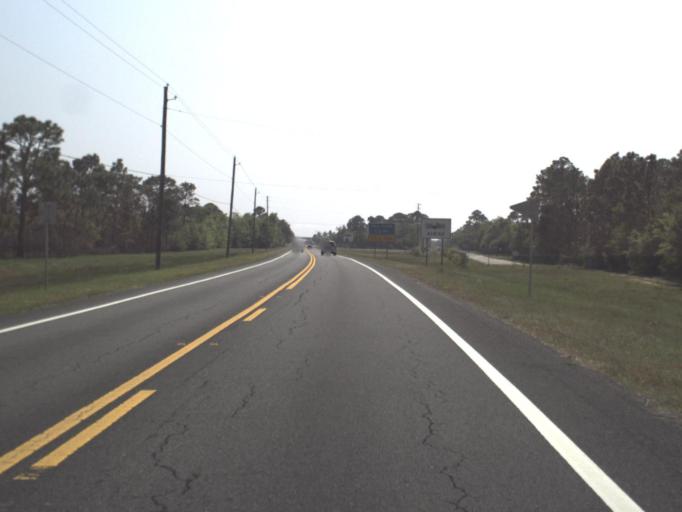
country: US
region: Florida
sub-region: Santa Rosa County
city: Oriole Beach
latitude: 30.4632
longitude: -87.0906
